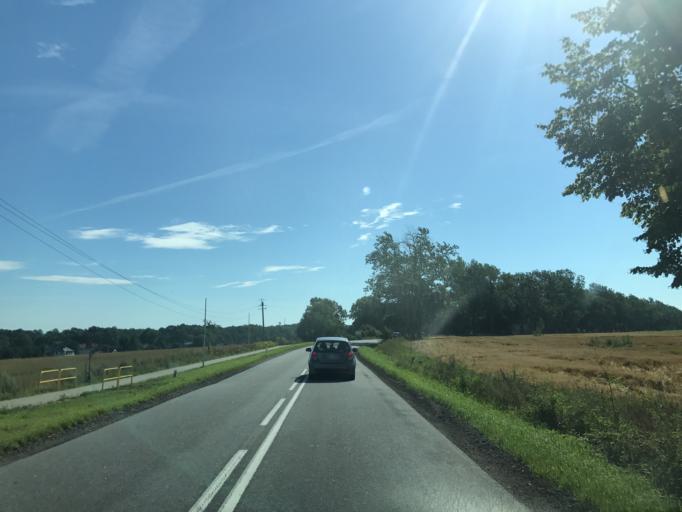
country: PL
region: Pomeranian Voivodeship
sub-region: Powiat slupski
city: Potegowo
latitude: 54.4174
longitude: 17.4044
